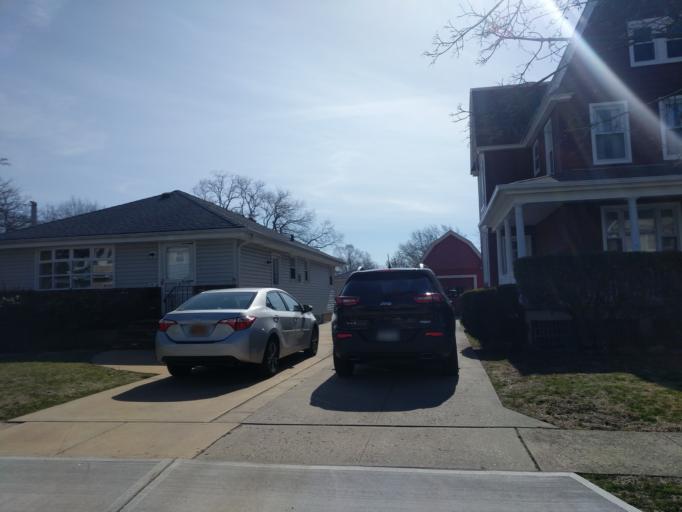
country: US
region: New York
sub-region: Nassau County
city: Hewlett
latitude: 40.6563
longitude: -73.6945
